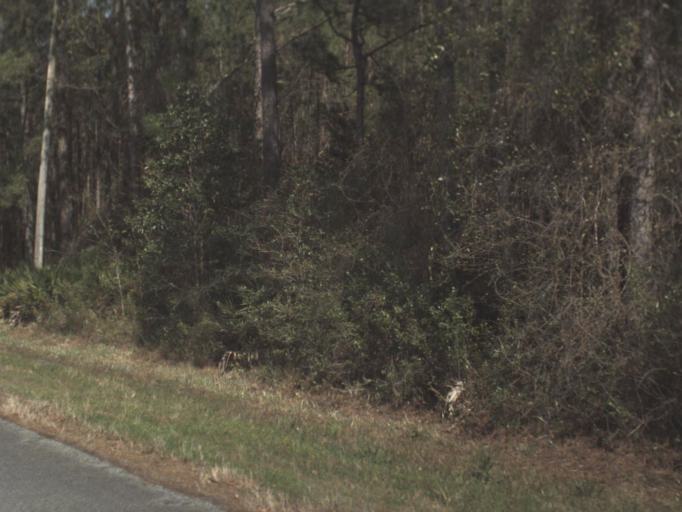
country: US
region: Florida
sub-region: Franklin County
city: Carrabelle
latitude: 29.9642
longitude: -84.5011
